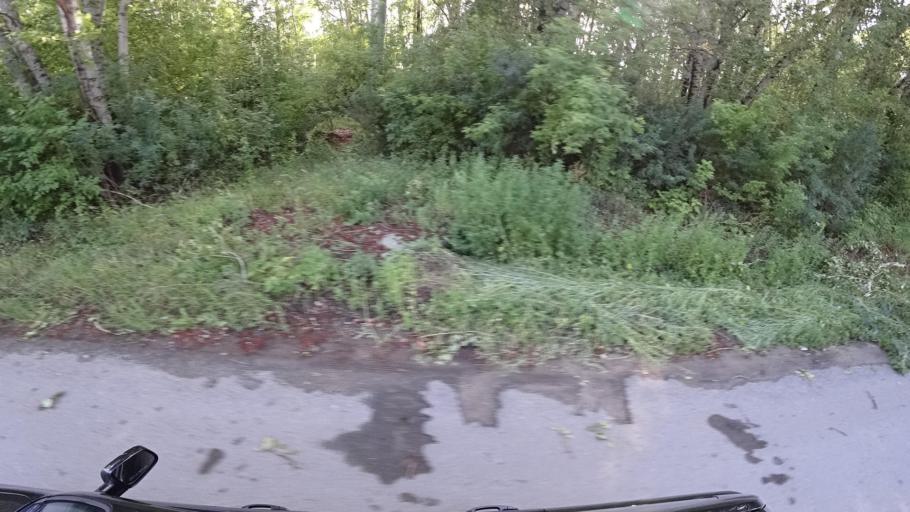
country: RU
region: Sverdlovsk
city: Obukhovskoye
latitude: 56.8480
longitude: 62.6540
